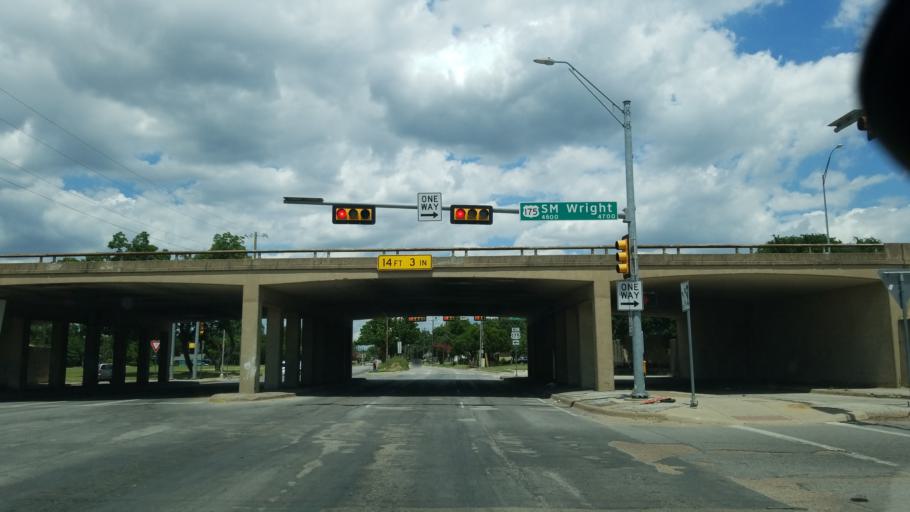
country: US
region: Texas
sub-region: Dallas County
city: Dallas
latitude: 32.7492
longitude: -96.7615
